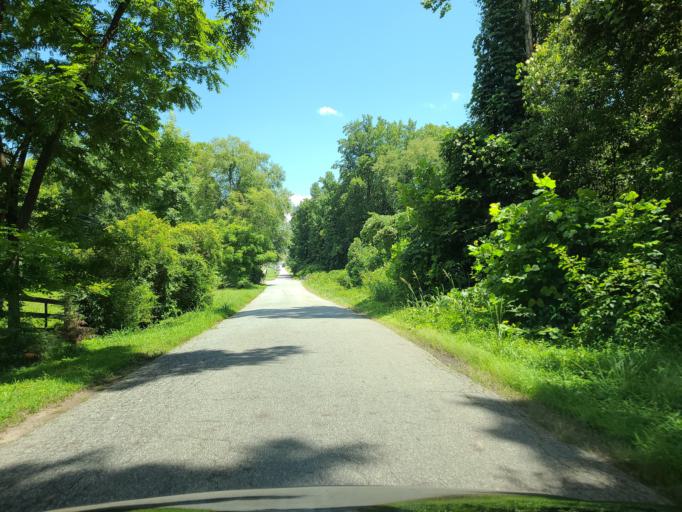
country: US
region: South Carolina
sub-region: Spartanburg County
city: Inman Mills
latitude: 35.0418
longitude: -82.1596
